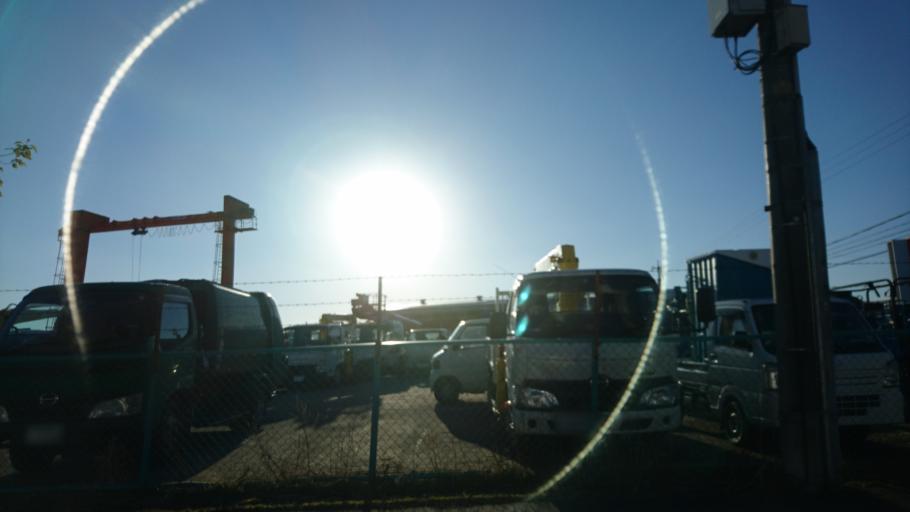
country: JP
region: Mie
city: Ueno-ebisumachi
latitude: 34.7525
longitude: 136.1411
